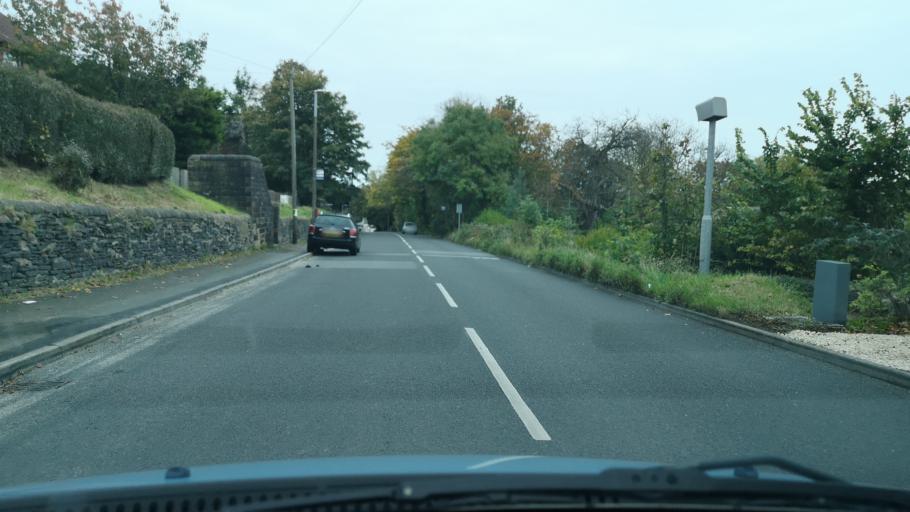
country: GB
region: England
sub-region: Kirklees
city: Heckmondwike
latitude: 53.6985
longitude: -1.6606
